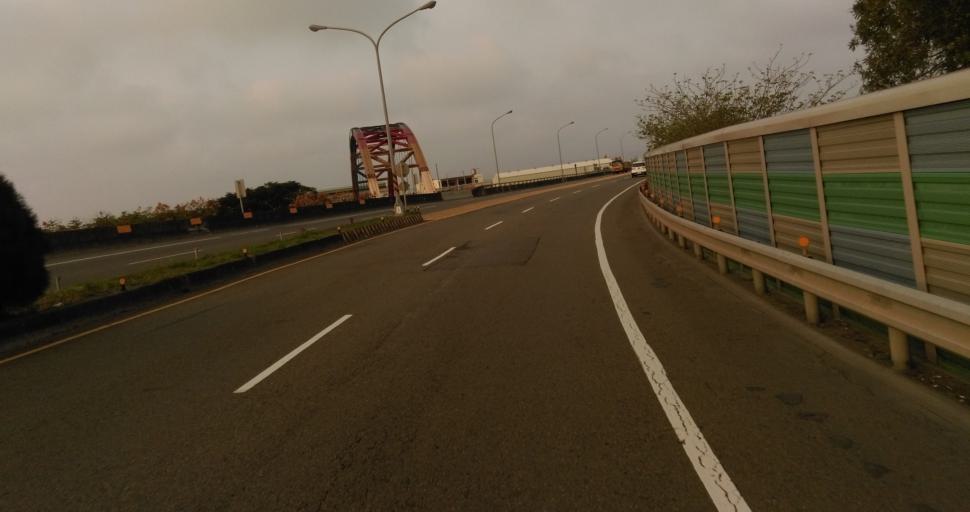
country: TW
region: Taiwan
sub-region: Hsinchu
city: Hsinchu
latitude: 24.8085
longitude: 120.9185
